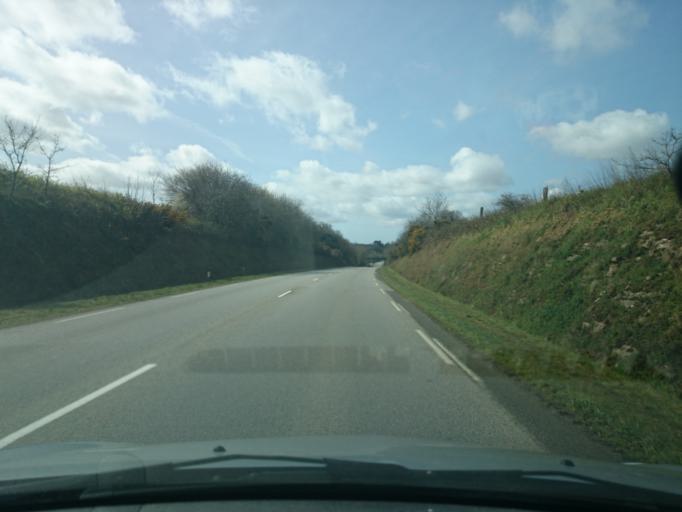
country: FR
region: Brittany
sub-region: Departement du Finistere
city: Gouesnou
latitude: 48.4526
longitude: -4.4488
